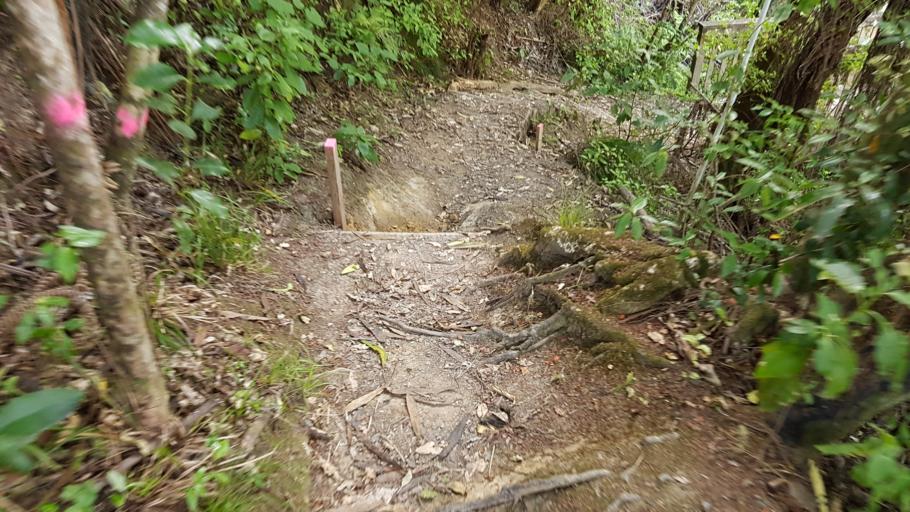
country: NZ
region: Auckland
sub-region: Auckland
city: North Shore
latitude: -36.8189
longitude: 174.7199
